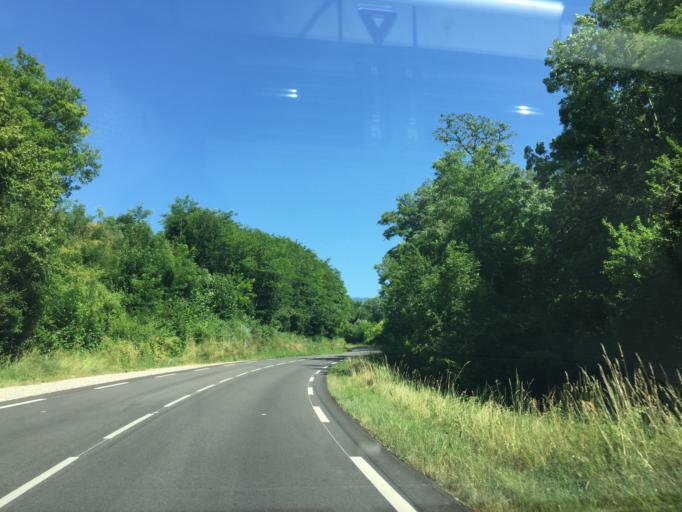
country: FR
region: Rhone-Alpes
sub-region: Departement de l'Isere
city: Saint-Just-de-Claix
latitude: 45.0541
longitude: 5.2603
